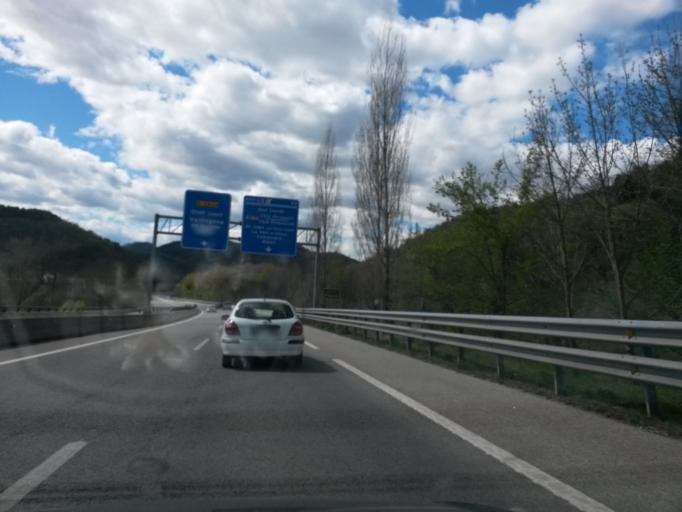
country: ES
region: Catalonia
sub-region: Provincia de Girona
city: Sant Joan les Fonts
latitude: 42.1941
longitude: 2.5103
